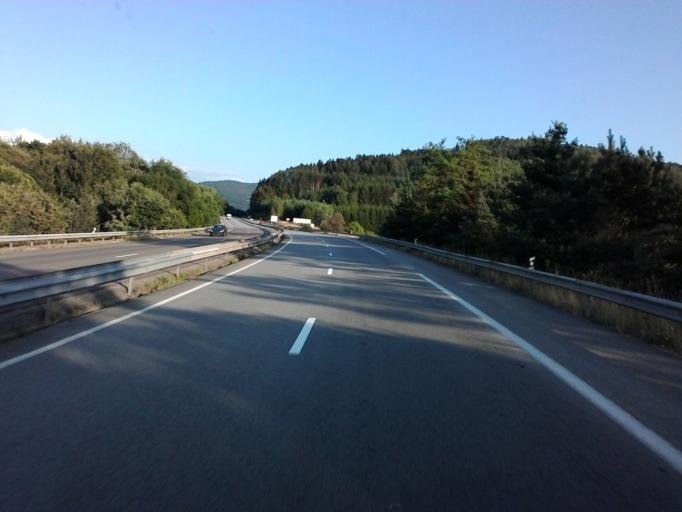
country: FR
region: Lorraine
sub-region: Departement des Vosges
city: Eloyes
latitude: 48.0957
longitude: 6.5906
